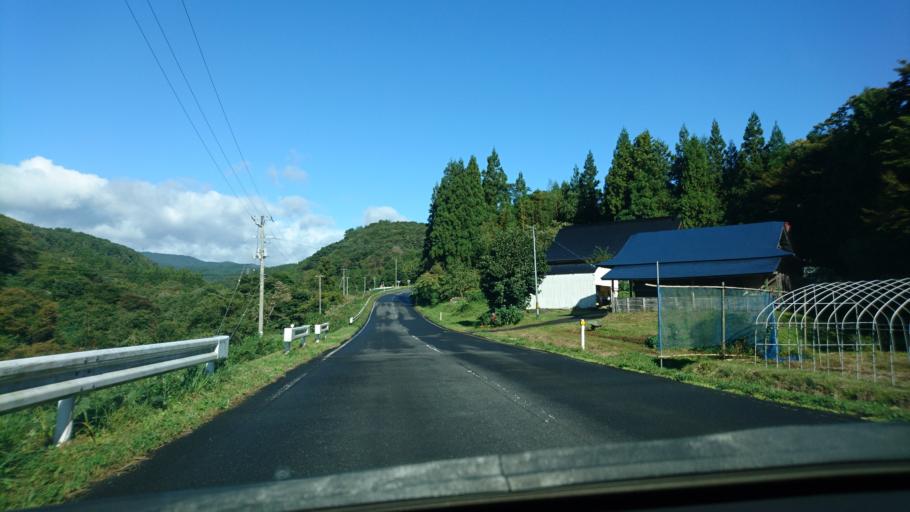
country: JP
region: Iwate
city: Ichinoseki
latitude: 39.0222
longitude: 141.0207
